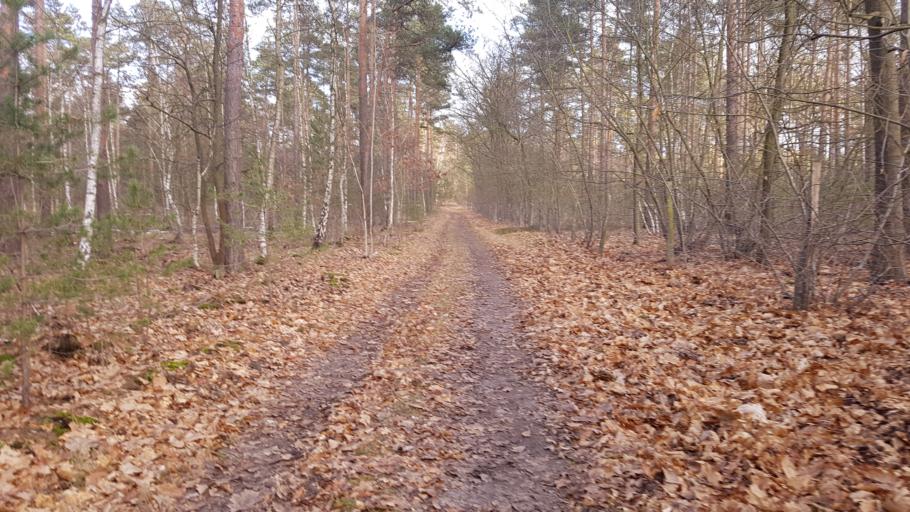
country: DE
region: Brandenburg
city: Stahnsdorf
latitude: 52.3491
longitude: 13.1588
